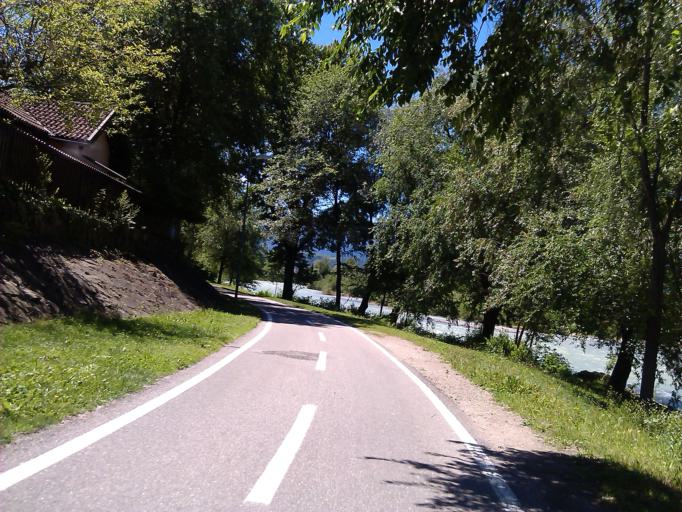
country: IT
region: Trentino-Alto Adige
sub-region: Bolzano
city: Bolzano
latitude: 46.4933
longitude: 11.3511
